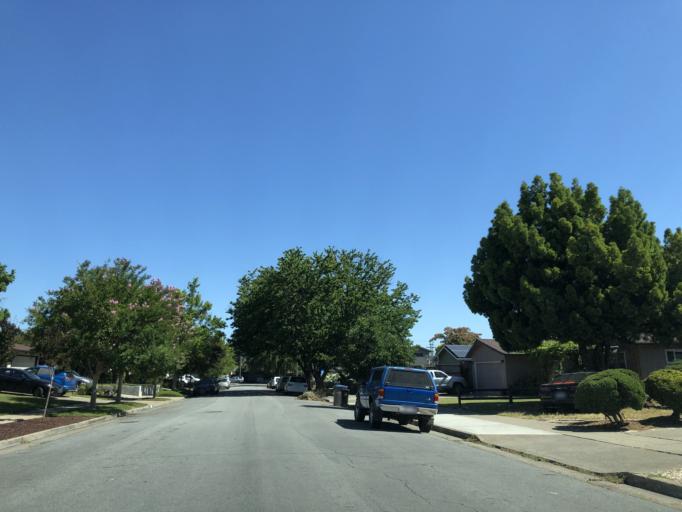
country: US
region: California
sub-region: Santa Clara County
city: Cambrian Park
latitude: 37.2414
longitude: -121.9276
